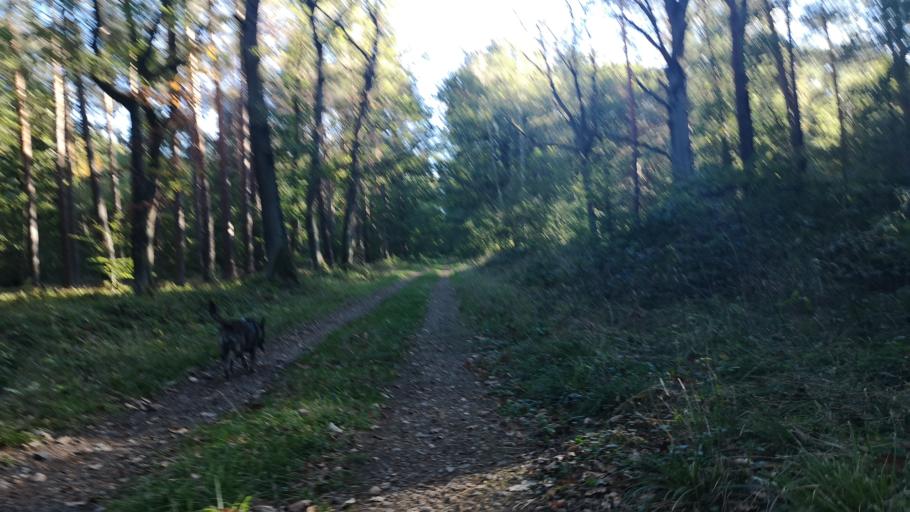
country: DE
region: North Rhine-Westphalia
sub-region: Regierungsbezirk Koln
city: Kreuzau
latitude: 50.7474
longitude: 6.5159
